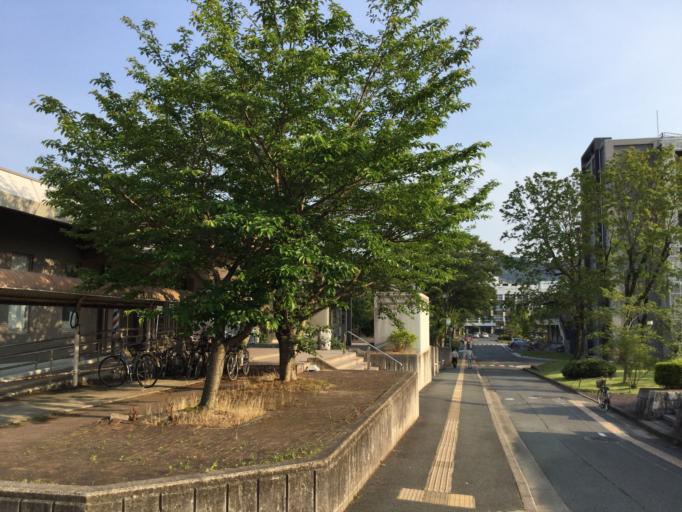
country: JP
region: Yamaguchi
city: Yamaguchi-shi
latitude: 34.1487
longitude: 131.4693
